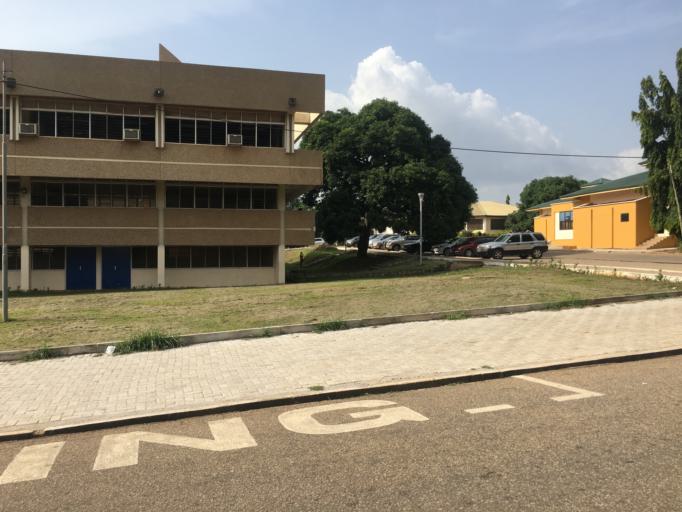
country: GH
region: Ashanti
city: Mamponteng
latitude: 6.6749
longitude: -1.5654
